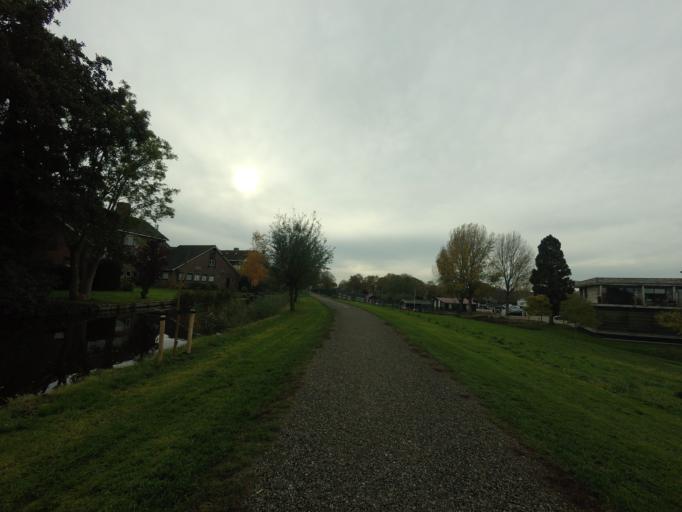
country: NL
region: South Holland
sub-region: Gemeente Nieuwkoop
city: Nieuwkoop
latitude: 52.1482
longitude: 4.7758
